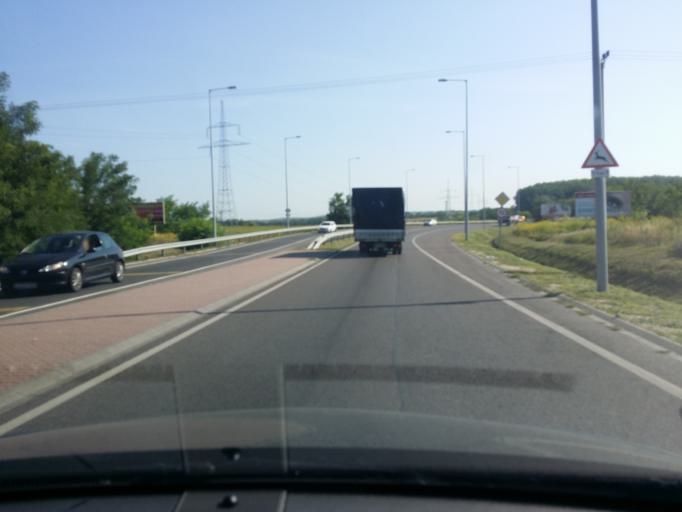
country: HU
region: Budapest
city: Budapest XVI. keruelet
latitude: 47.5432
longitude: 19.1702
